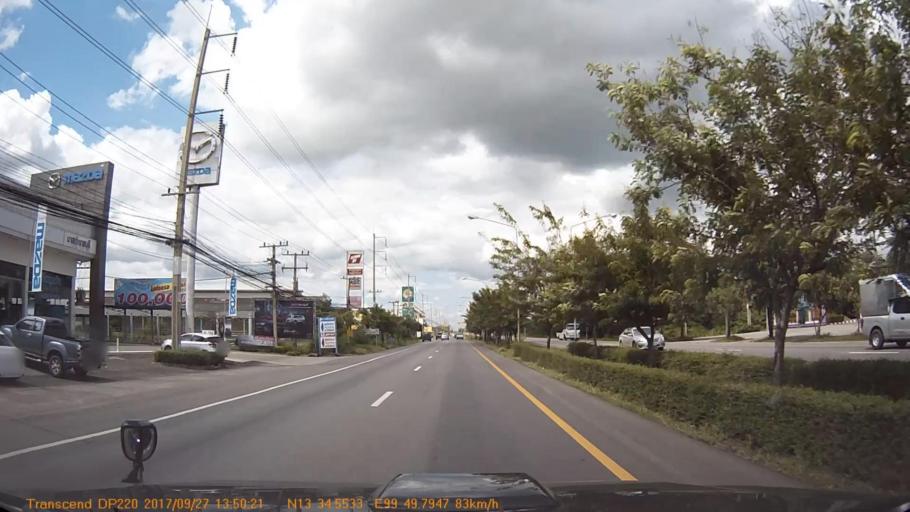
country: TH
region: Ratchaburi
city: Ratchaburi
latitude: 13.5761
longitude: 99.8299
